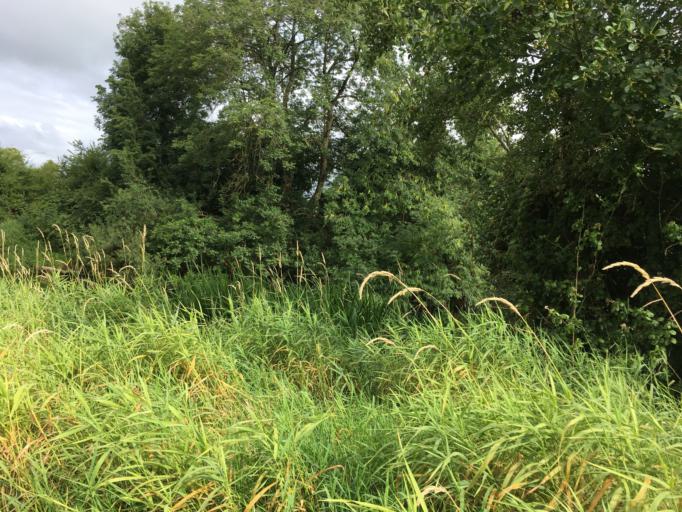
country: IE
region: Munster
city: Cashel
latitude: 52.4737
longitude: -7.9959
